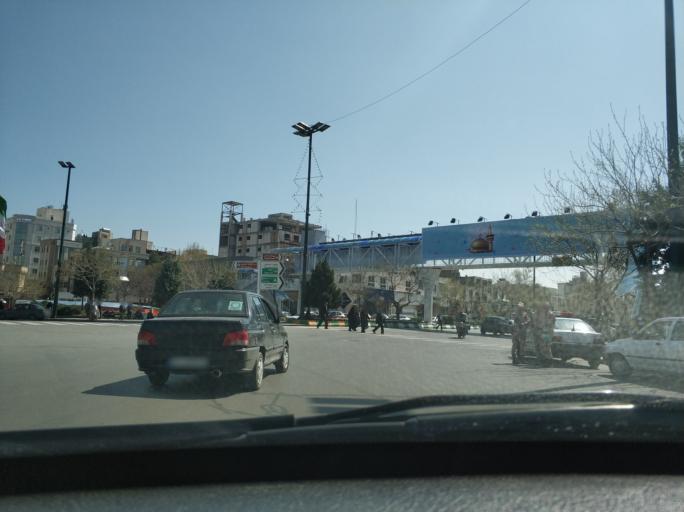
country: IR
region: Razavi Khorasan
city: Mashhad
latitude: 36.2676
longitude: 59.5988
